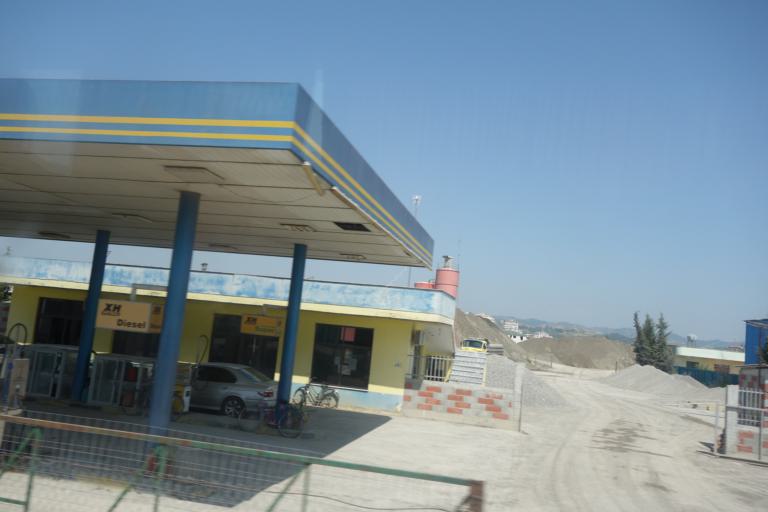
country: AL
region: Tirane
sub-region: Rrethi i Tiranes
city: Shengjergj
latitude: 41.1919
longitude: 19.5404
